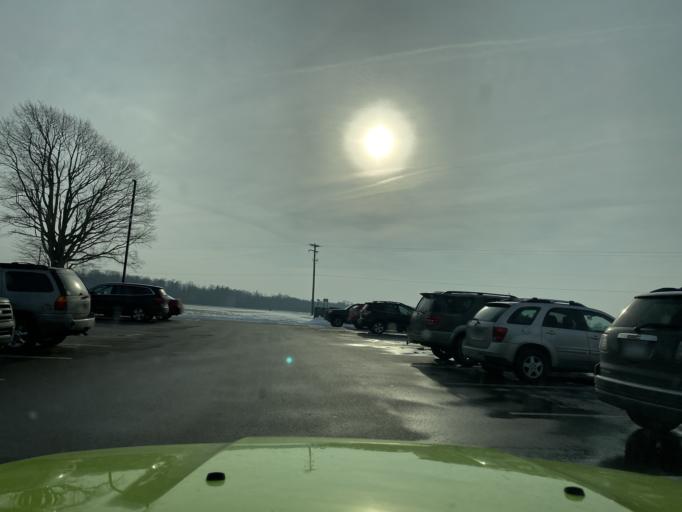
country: US
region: Michigan
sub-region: Ottawa County
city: Allendale
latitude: 42.9585
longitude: -85.9639
